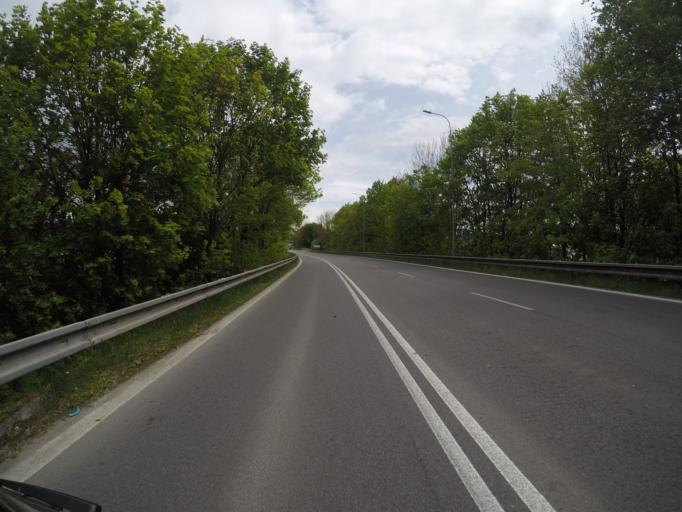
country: SK
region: Banskobystricky
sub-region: Okres Banska Bystrica
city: Banska Bystrica
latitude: 48.7385
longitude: 19.1757
